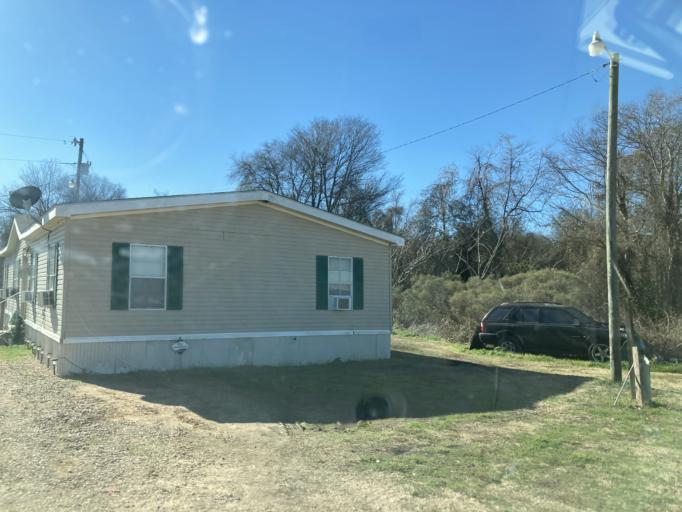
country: US
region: Mississippi
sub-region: Yazoo County
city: Yazoo City
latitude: 32.9701
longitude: -90.5963
